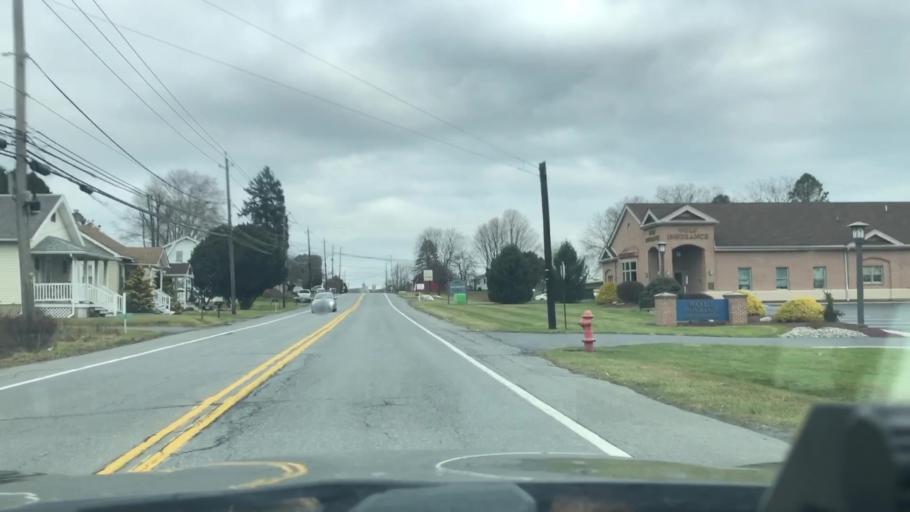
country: US
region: Pennsylvania
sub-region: Northampton County
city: Nazareth
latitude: 40.7250
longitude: -75.3171
